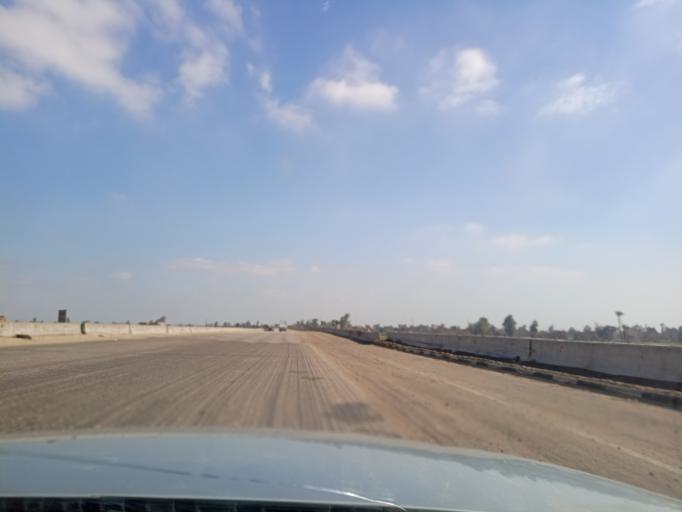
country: EG
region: Muhafazat al Minufiyah
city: Al Bajur
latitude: 30.4196
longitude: 31.0800
